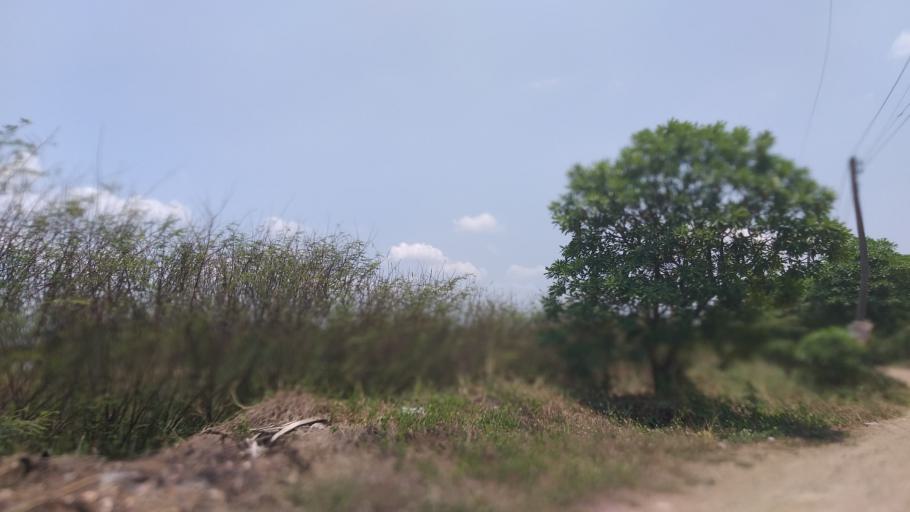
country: TH
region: Nakhon Nayok
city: Ongkharak
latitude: 14.0916
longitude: 100.9147
